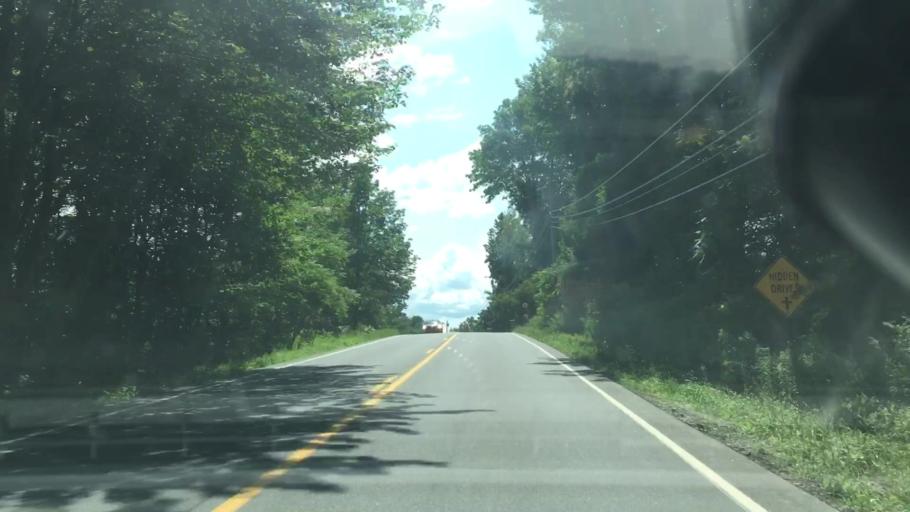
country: US
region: Maine
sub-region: Somerset County
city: Skowhegan
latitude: 44.6716
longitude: -69.6830
